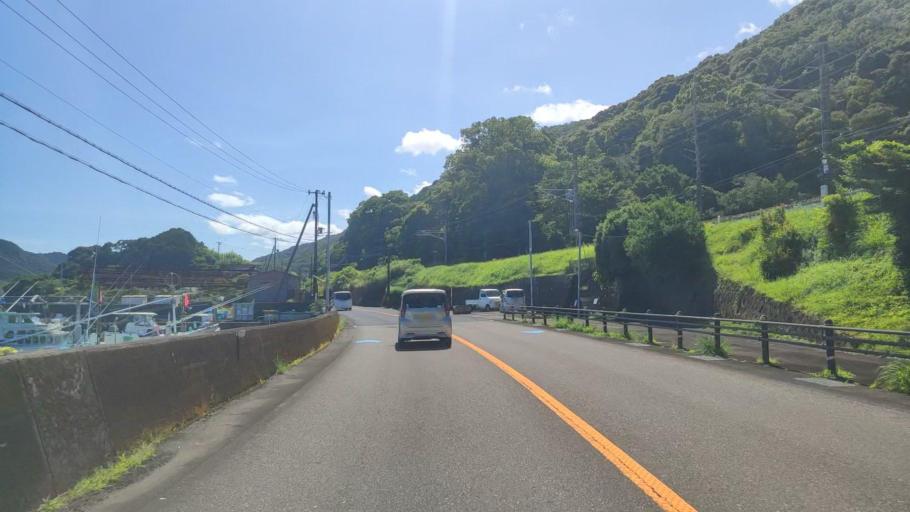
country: JP
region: Wakayama
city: Shingu
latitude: 33.5632
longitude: 135.8997
